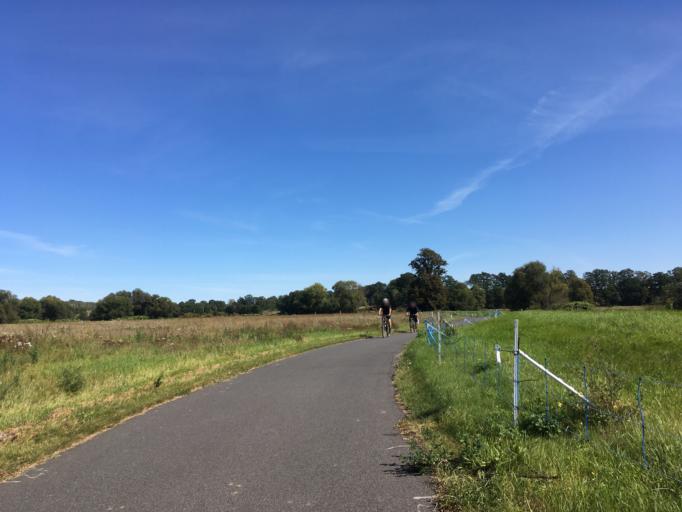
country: PL
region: Lower Silesian Voivodeship
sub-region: Powiat zgorzelecki
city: Piensk
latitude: 51.2145
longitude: 15.0124
